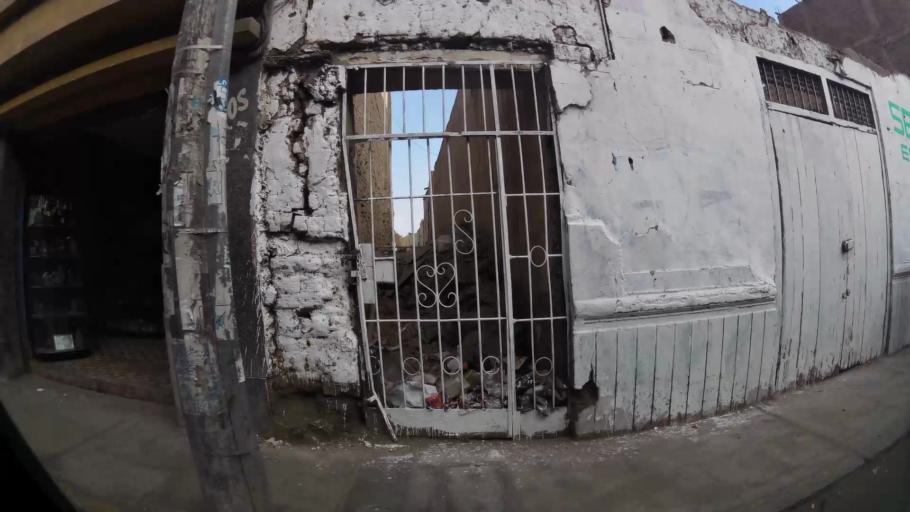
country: PE
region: La Libertad
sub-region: Provincia de Trujillo
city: Trujillo
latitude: -8.1073
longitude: -79.0203
